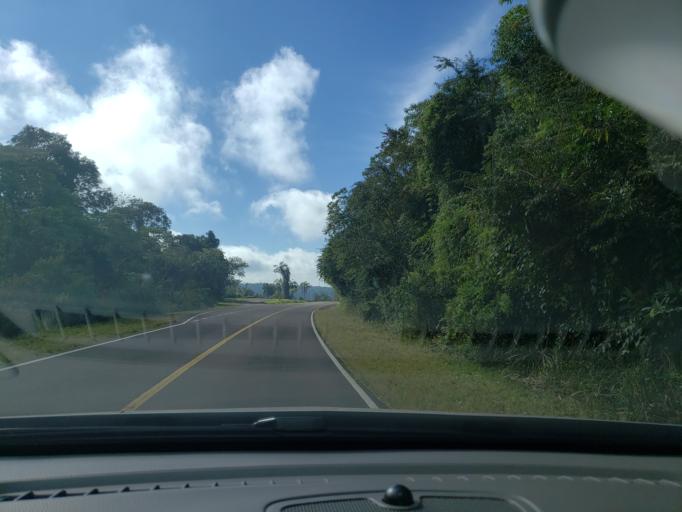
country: AR
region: Misiones
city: El Soberbio
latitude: -27.1243
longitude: -53.9485
